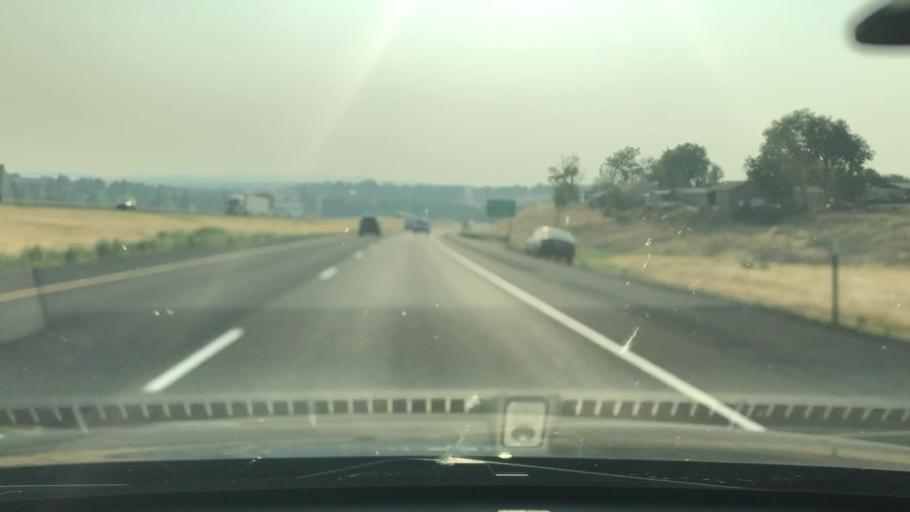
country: US
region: Oregon
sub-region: Umatilla County
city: Pendleton
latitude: 45.6614
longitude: -118.7933
